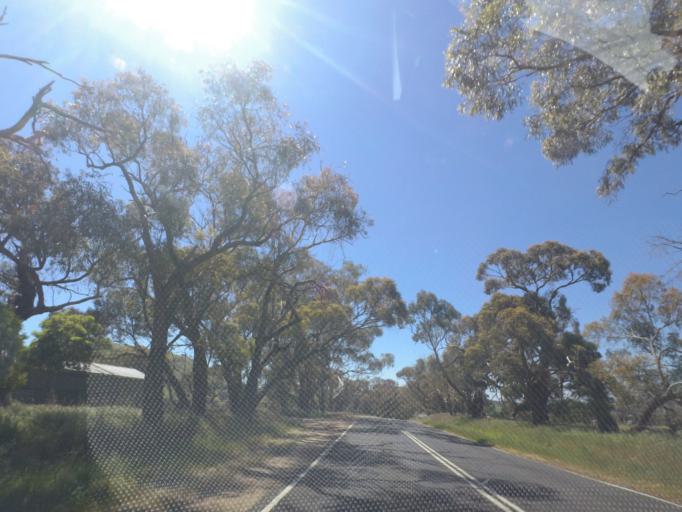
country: AU
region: Victoria
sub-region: Hume
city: Sunbury
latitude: -37.0654
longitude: 144.7808
